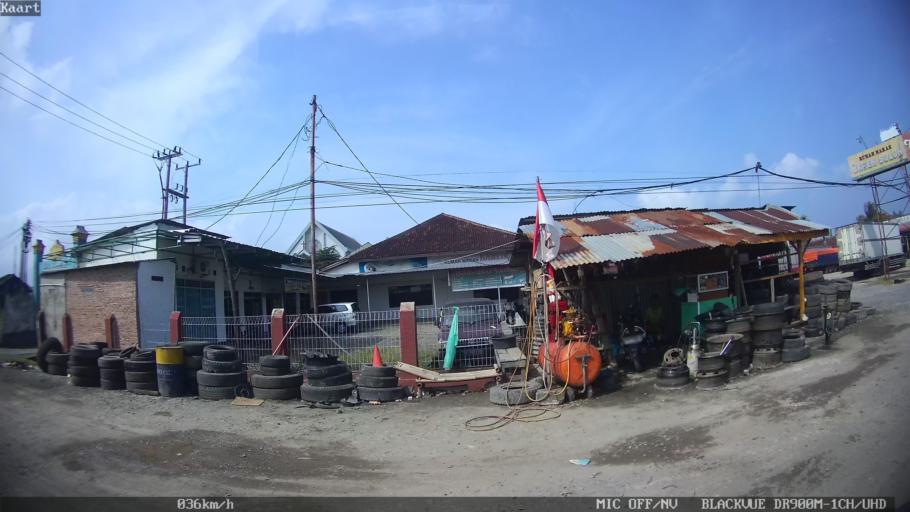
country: ID
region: Lampung
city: Kedaton
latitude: -5.3604
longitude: 105.2557
